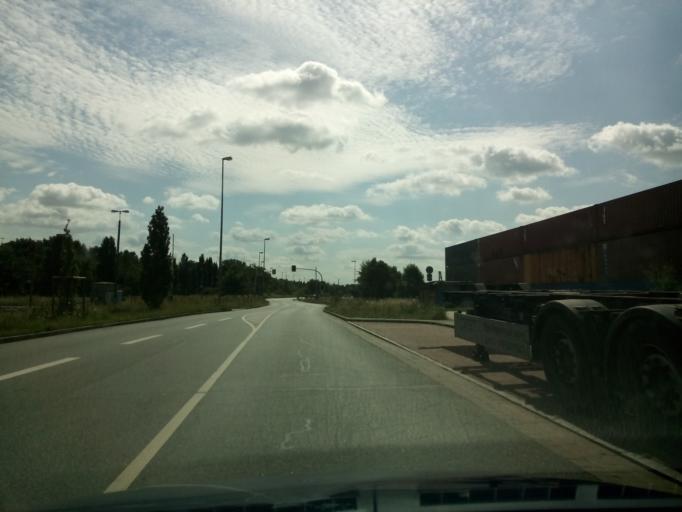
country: DE
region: Lower Saxony
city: Ritterhude
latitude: 53.1243
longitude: 8.7401
